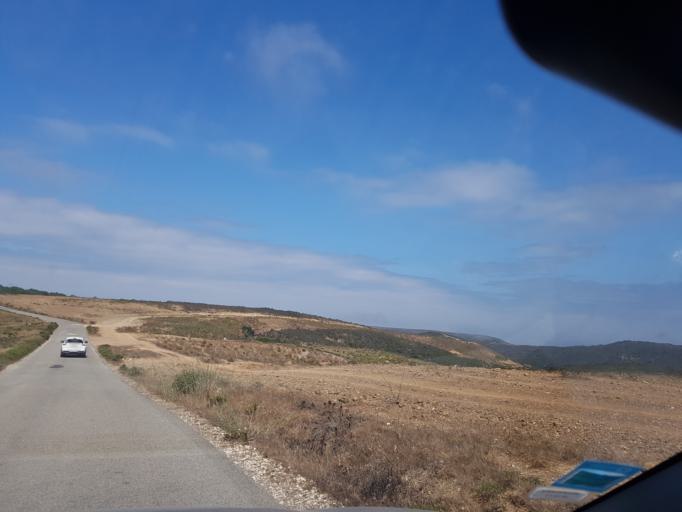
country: PT
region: Faro
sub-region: Vila do Bispo
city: Vila do Bispo
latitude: 37.0900
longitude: -8.9243
